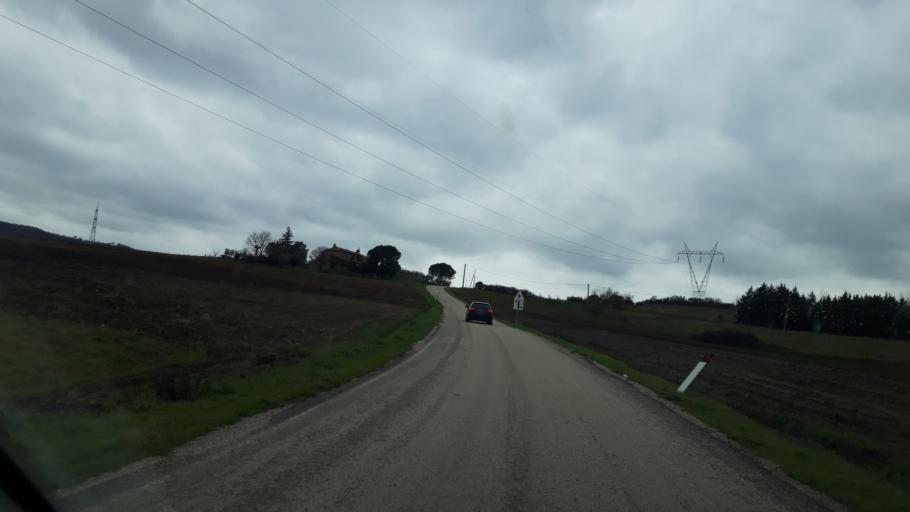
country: IT
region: Umbria
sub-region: Provincia di Perugia
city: Tavernelle
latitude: 42.9889
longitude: 12.1769
